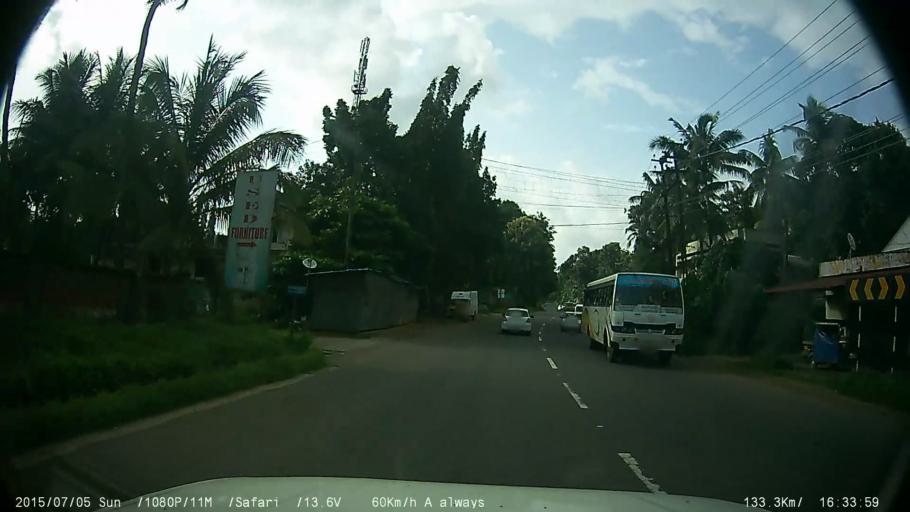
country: IN
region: Kerala
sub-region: Ernakulam
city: Muvattupula
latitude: 9.9998
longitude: 76.5715
